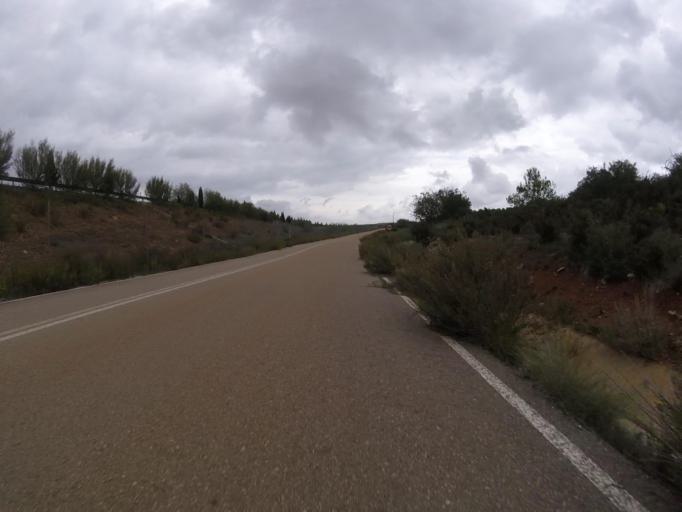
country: ES
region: Valencia
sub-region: Provincia de Castello
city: Benlloch
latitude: 40.1909
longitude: 0.0485
